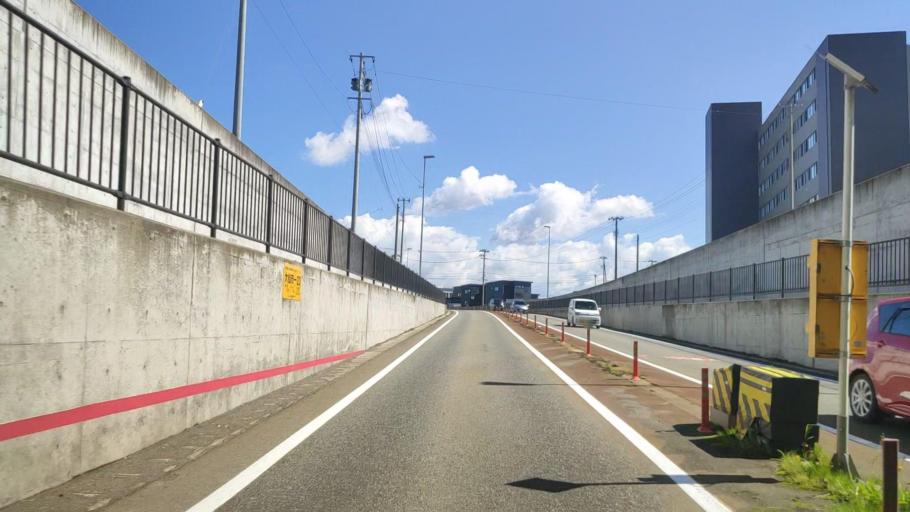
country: JP
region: Akita
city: Omagari
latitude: 39.4624
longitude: 140.4830
